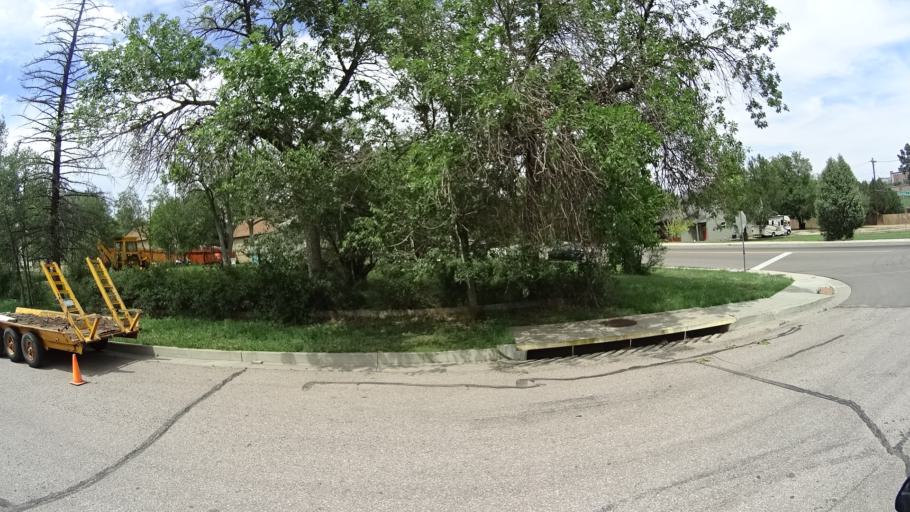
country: US
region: Colorado
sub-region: El Paso County
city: Colorado Springs
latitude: 38.8608
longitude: -104.8365
